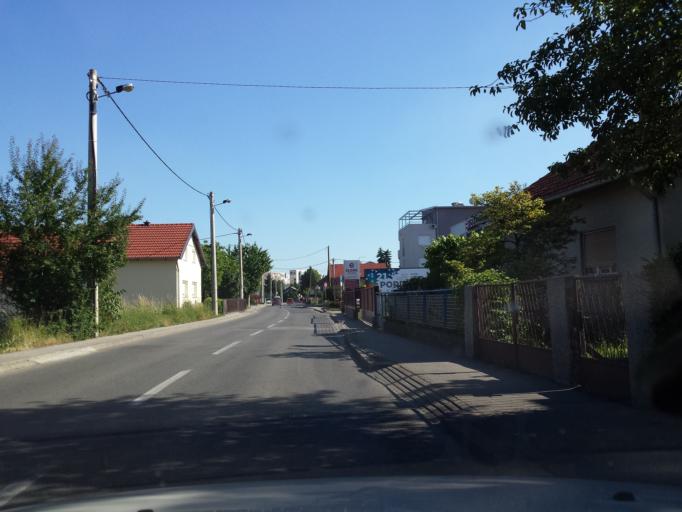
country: HR
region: Grad Zagreb
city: Jankomir
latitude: 45.8049
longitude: 15.9084
